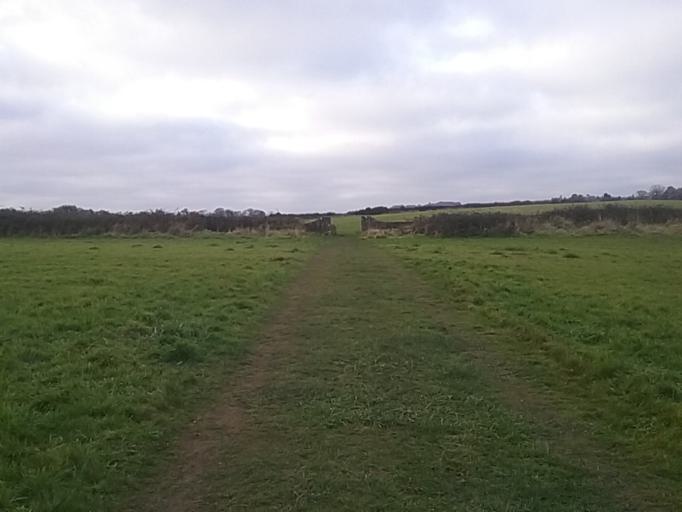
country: IE
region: Leinster
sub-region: Lu
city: Tullyallen
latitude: 53.7178
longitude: -6.4116
